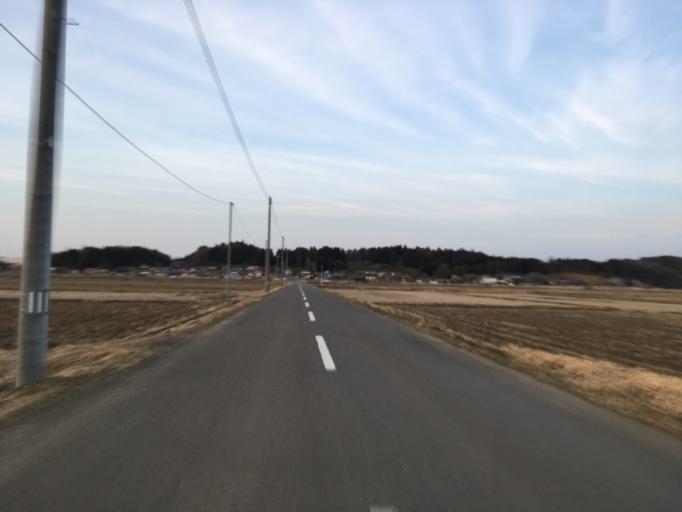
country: JP
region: Fukushima
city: Ishikawa
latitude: 37.0593
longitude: 140.3480
